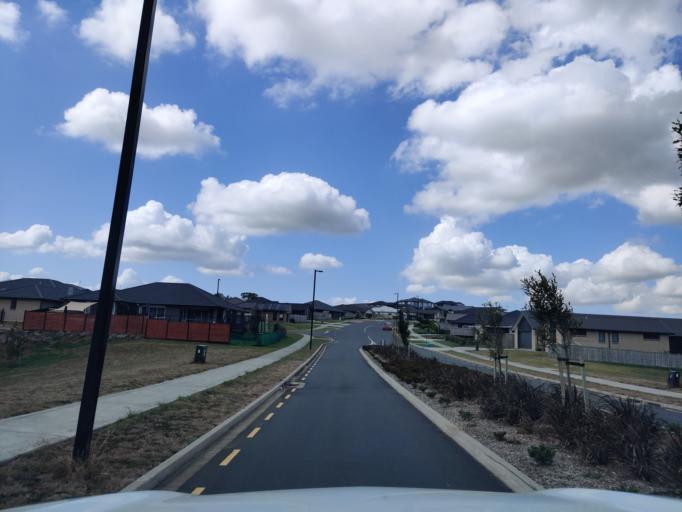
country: NZ
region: Auckland
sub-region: Auckland
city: Pukekohe East
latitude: -37.2362
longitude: 175.0171
